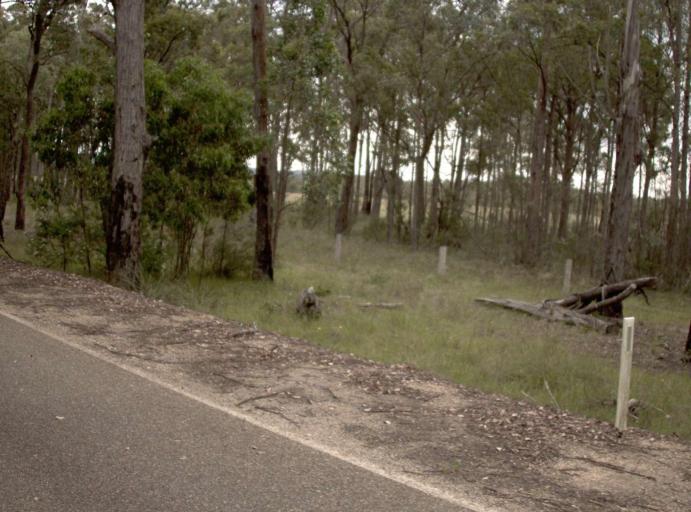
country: AU
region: Victoria
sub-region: East Gippsland
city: Bairnsdale
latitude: -37.7492
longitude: 147.3232
